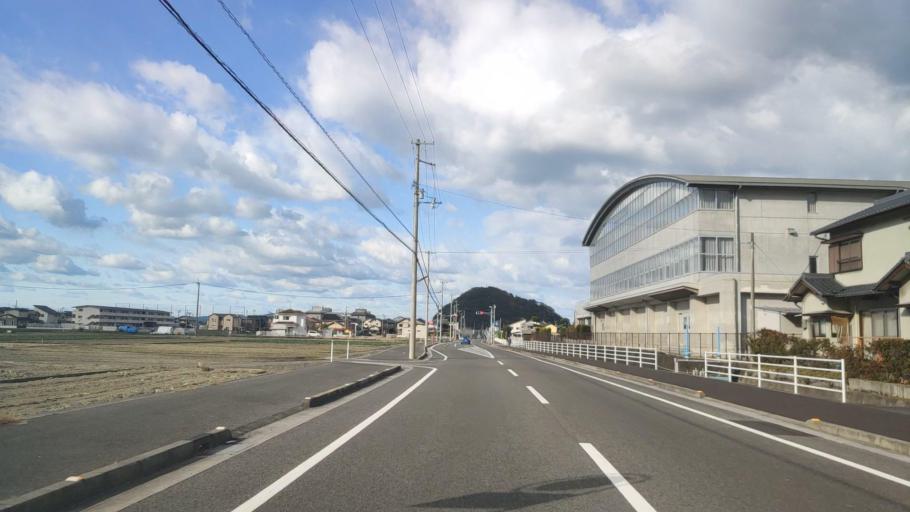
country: JP
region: Ehime
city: Hojo
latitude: 33.9700
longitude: 132.7817
